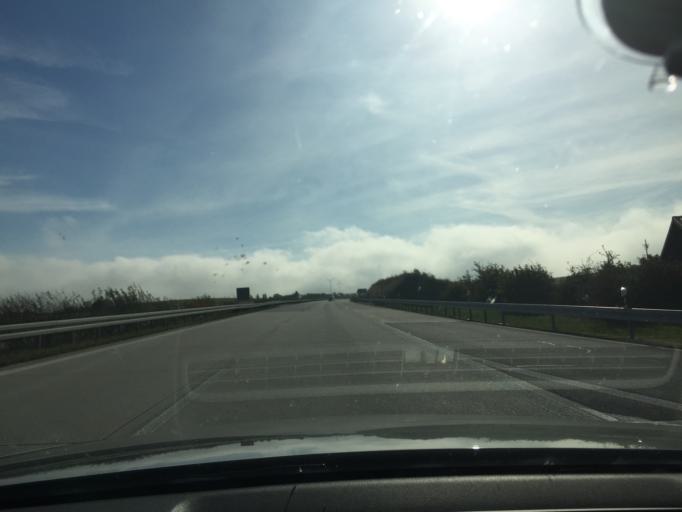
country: DE
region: Saxony
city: Liebstadt
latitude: 50.8321
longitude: 13.8854
